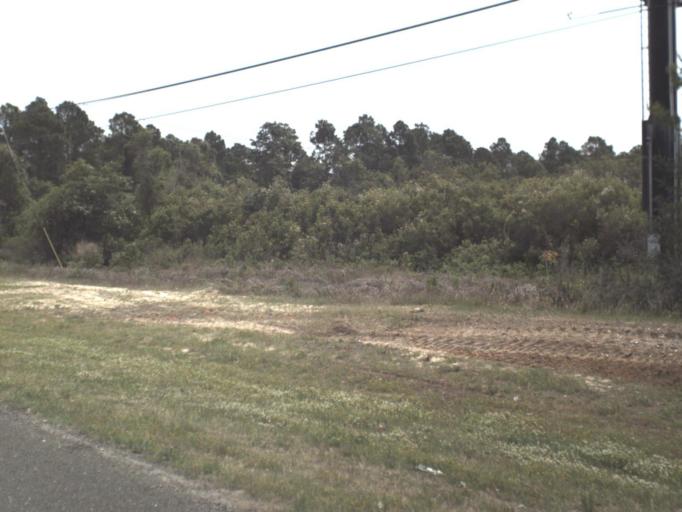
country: US
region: Florida
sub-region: Santa Rosa County
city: Holley
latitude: 30.4019
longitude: -86.9107
